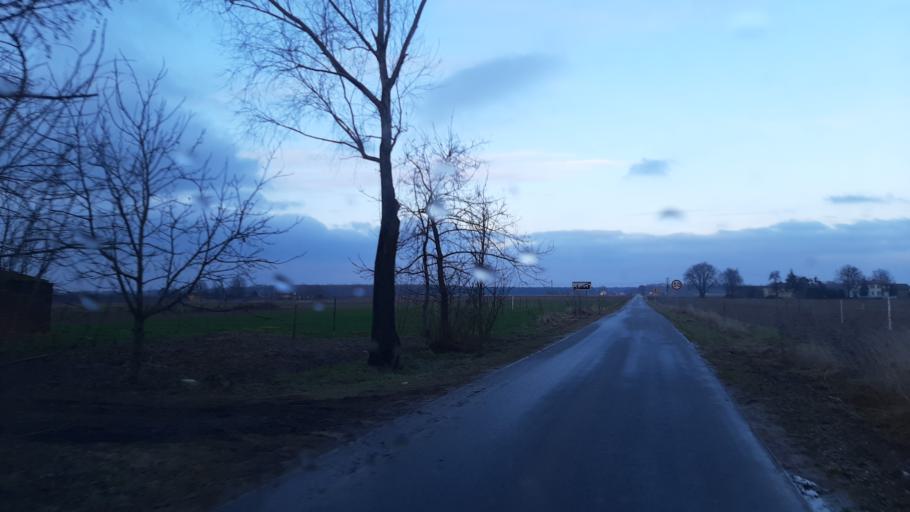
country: PL
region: Lublin Voivodeship
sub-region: Powiat lubelski
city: Jastkow
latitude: 51.3557
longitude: 22.3951
